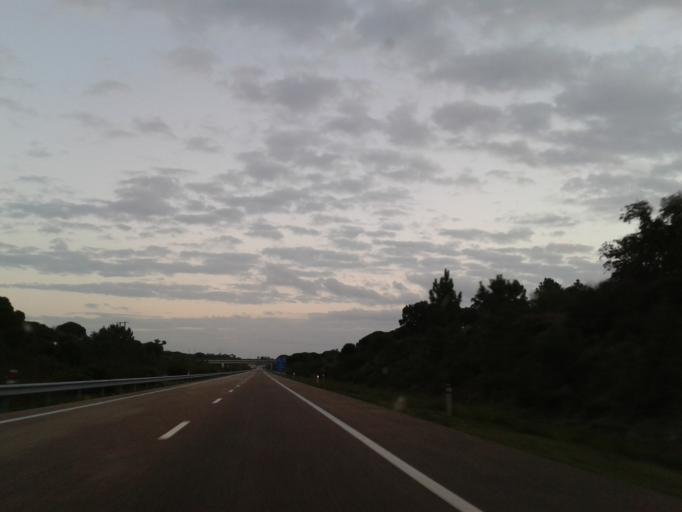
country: PT
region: Evora
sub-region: Vendas Novas
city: Vendas Novas
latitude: 38.6247
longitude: -8.6571
